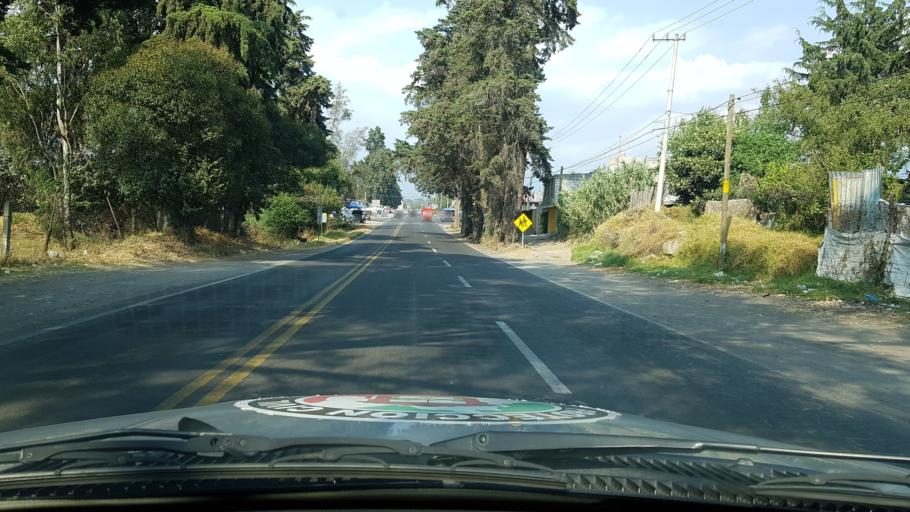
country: MX
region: Mexico
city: Ozumba de Alzate
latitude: 19.0435
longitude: -98.7988
